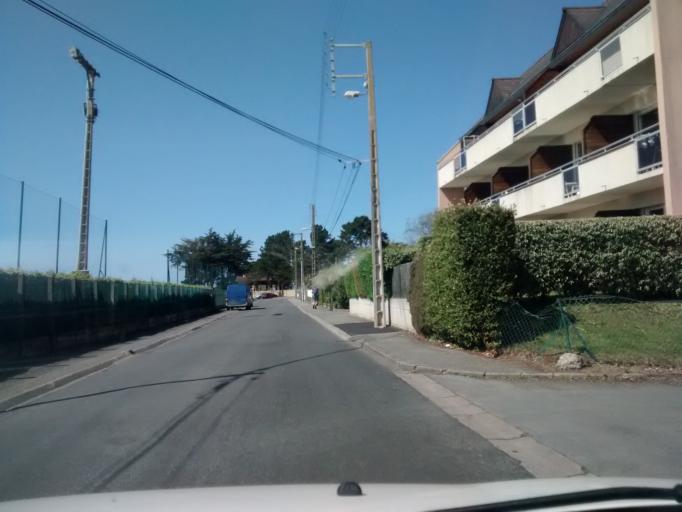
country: FR
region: Brittany
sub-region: Departement d'Ille-et-Vilaine
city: Dinard
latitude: 48.6336
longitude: -2.0773
